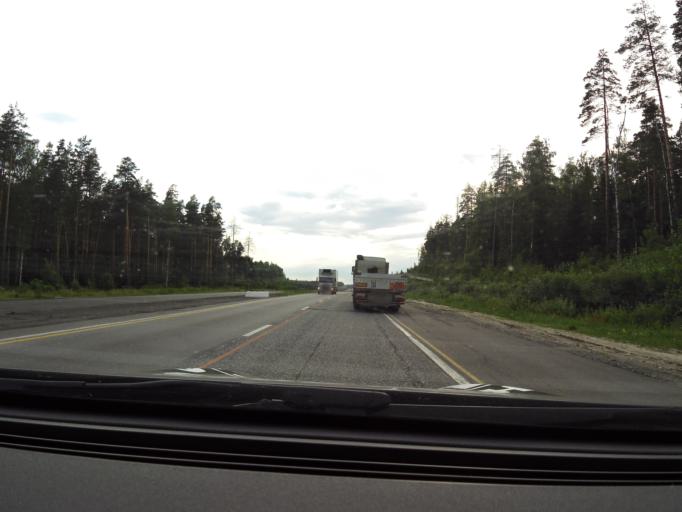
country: RU
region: Vladimir
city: Orgtrud
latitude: 56.1036
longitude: 40.6718
